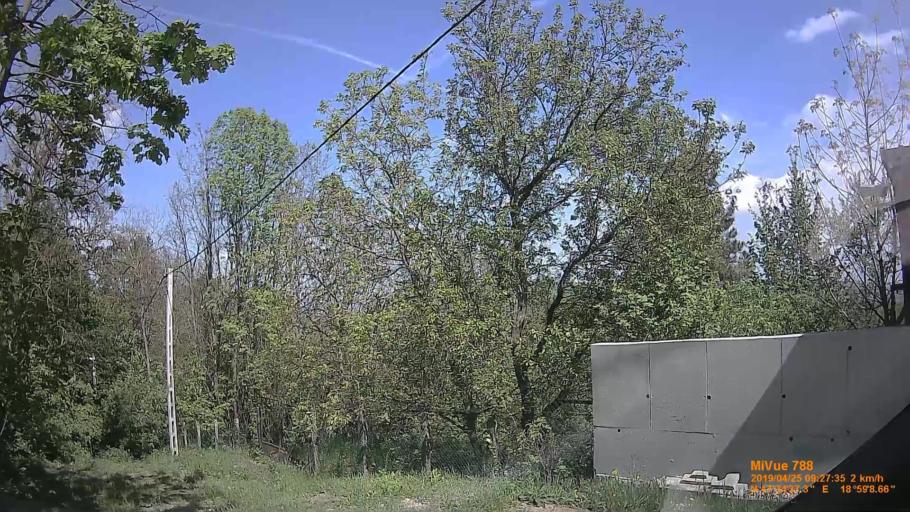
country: HU
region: Pest
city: Pilisborosjeno
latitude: 47.5770
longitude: 18.9858
